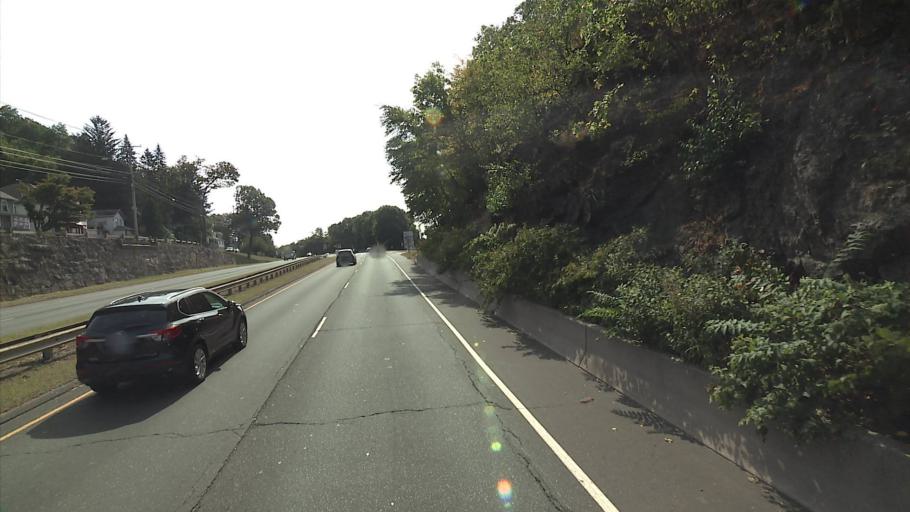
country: US
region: Connecticut
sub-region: New Haven County
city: Derby
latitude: 41.3118
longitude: -73.0766
